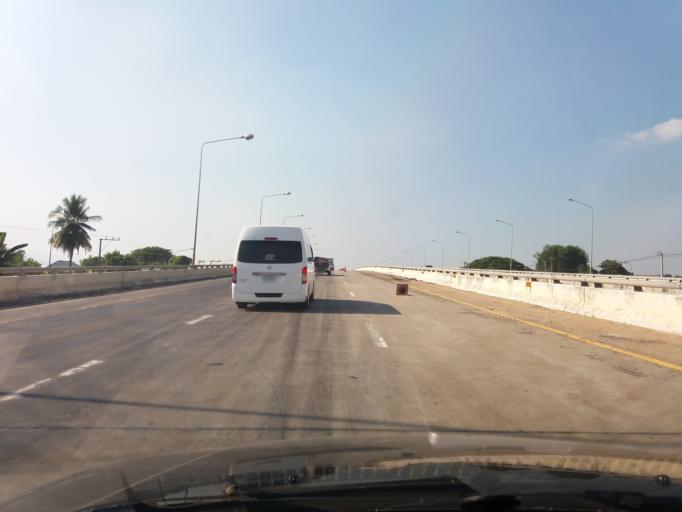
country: TH
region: Nakhon Sawan
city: Nakhon Sawan
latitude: 15.6318
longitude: 100.1029
